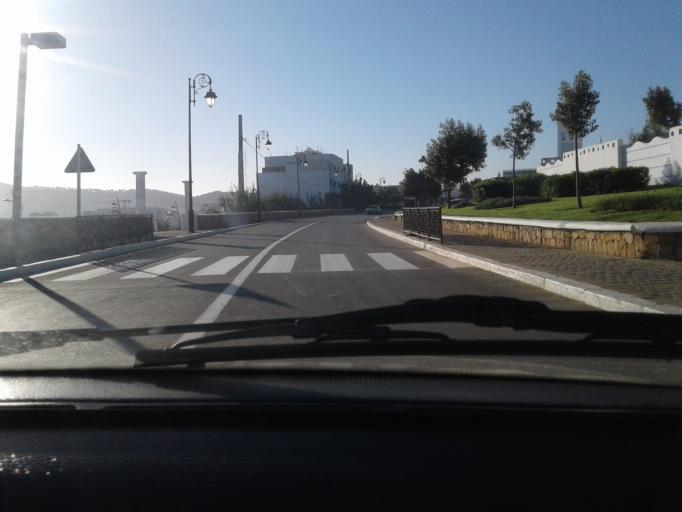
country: MA
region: Tanger-Tetouan
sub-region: Tetouan
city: Martil
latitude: 35.6911
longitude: -5.3308
